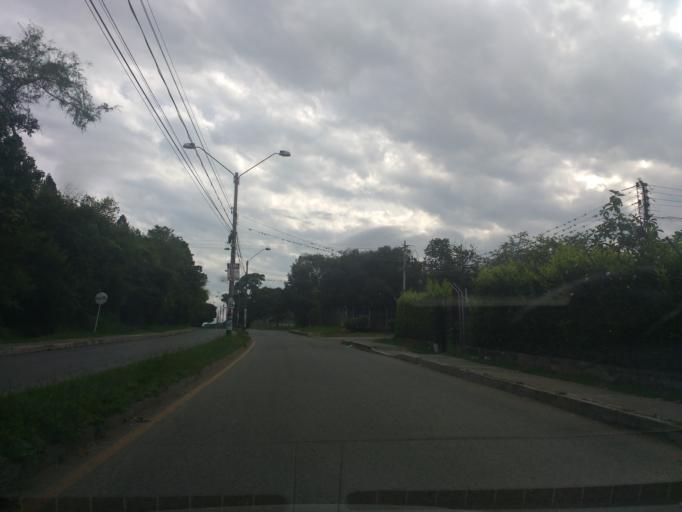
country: CO
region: Cauca
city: Miranda
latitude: 3.2623
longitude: -76.2264
